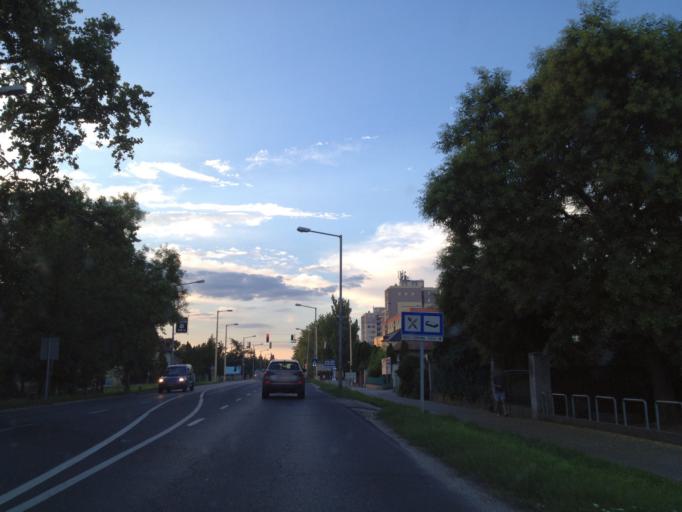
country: HU
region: Gyor-Moson-Sopron
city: Mosonmagyarovar
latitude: 47.8605
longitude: 17.2752
